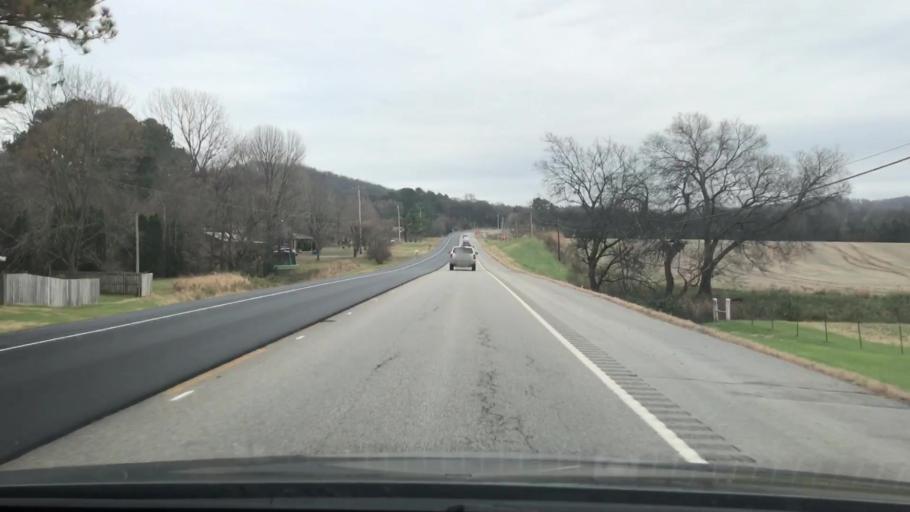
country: US
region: Tennessee
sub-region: Smith County
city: Carthage
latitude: 36.3361
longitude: -86.0279
